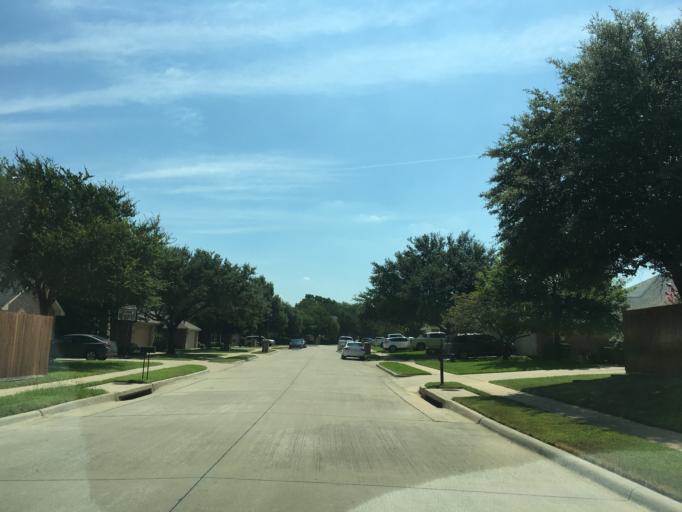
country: US
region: Texas
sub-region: Denton County
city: Lewisville
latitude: 33.0152
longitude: -97.0097
